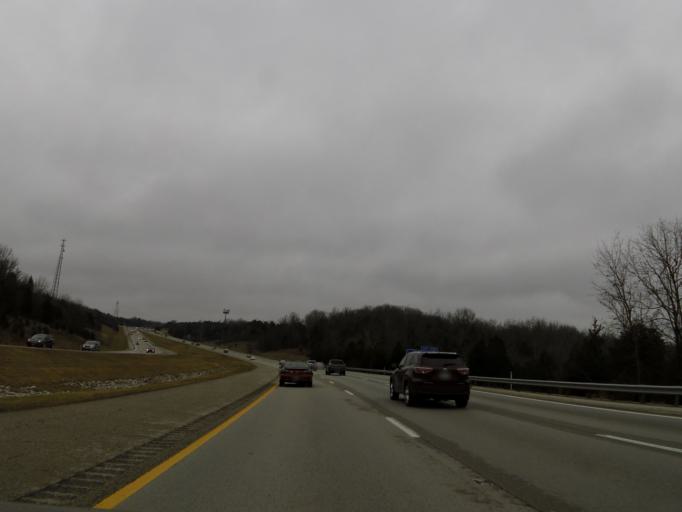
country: US
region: Kentucky
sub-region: Scott County
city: Georgetown
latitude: 38.3892
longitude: -84.5760
